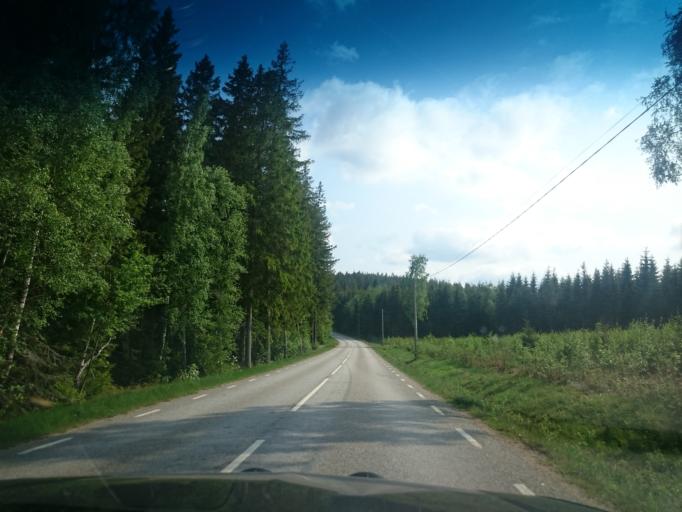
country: SE
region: Joenkoeping
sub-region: Vetlanda Kommun
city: Vetlanda
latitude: 57.3383
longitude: 15.0757
